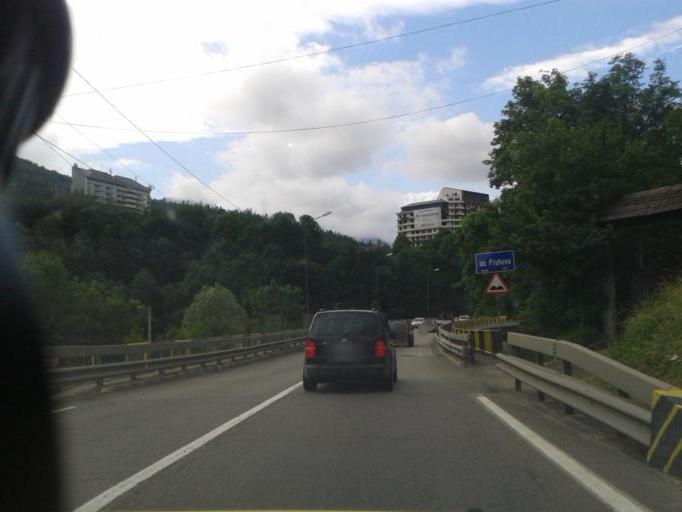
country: RO
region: Prahova
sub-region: Oras Sinaia
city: Sinaia
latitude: 45.3182
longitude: 25.5641
